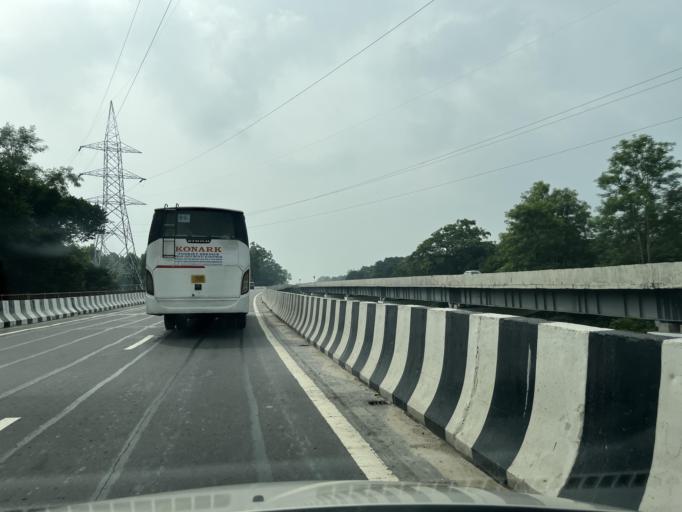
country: IN
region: Uttarakhand
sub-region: Dehradun
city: Raiwala
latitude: 30.0692
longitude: 78.2068
